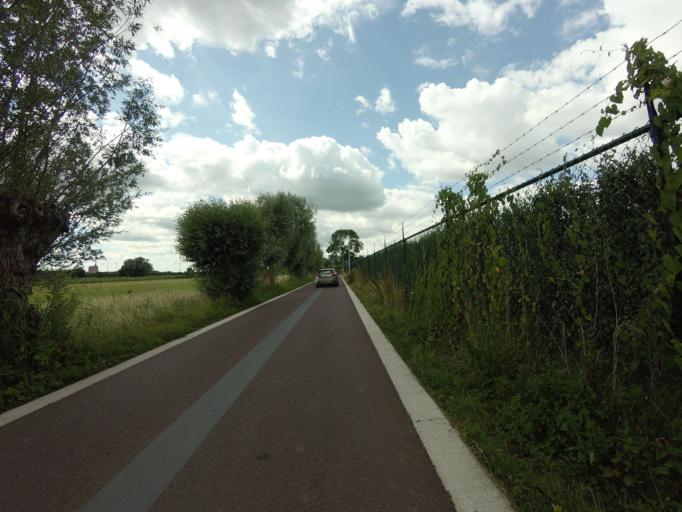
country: NL
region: Utrecht
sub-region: Gemeente Utrecht
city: Lunetten
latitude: 52.0410
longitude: 5.1264
